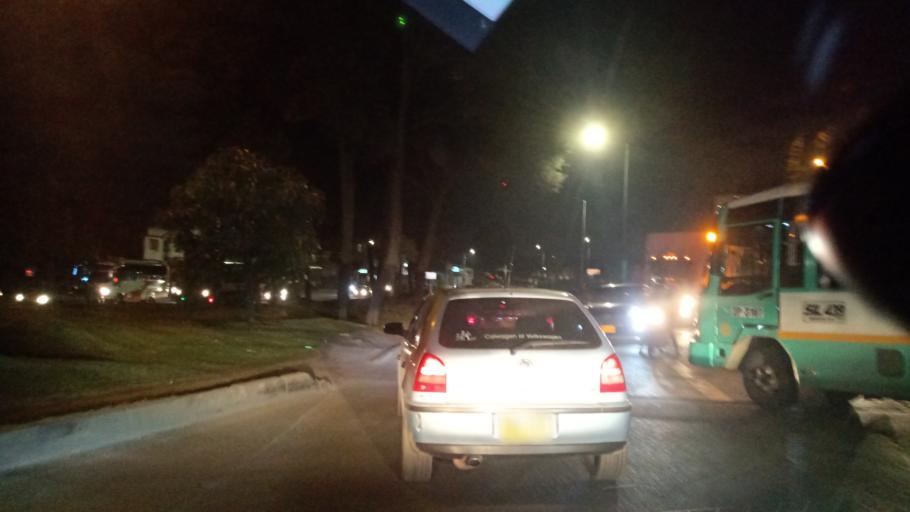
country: CO
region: Cundinamarca
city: Funza
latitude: 4.6857
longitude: -74.1584
